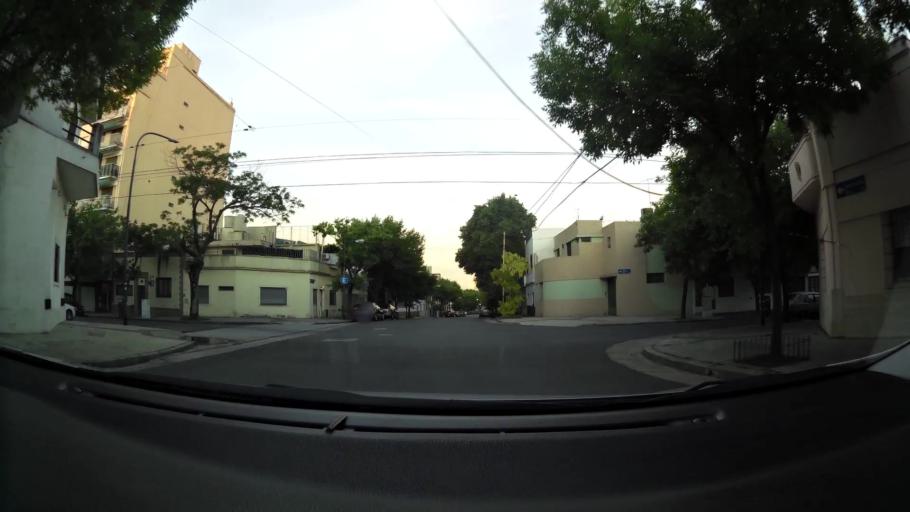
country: AR
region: Buenos Aires F.D.
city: Villa Santa Rita
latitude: -34.6374
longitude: -58.4398
